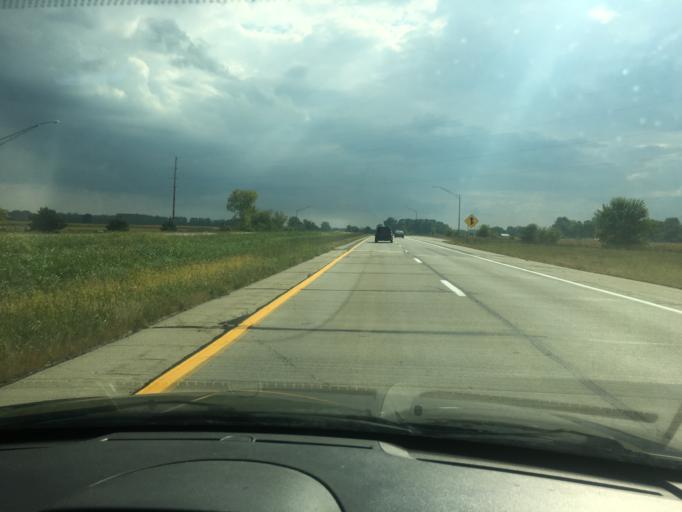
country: US
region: Ohio
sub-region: Clark County
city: Northridge
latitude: 40.0257
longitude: -83.8050
